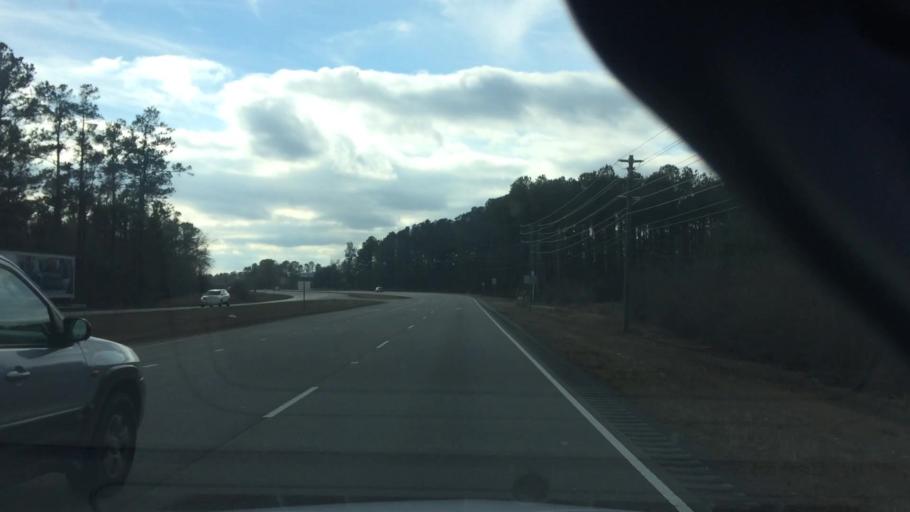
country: US
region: North Carolina
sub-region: Brunswick County
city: Bolivia
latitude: 34.1287
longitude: -78.1020
